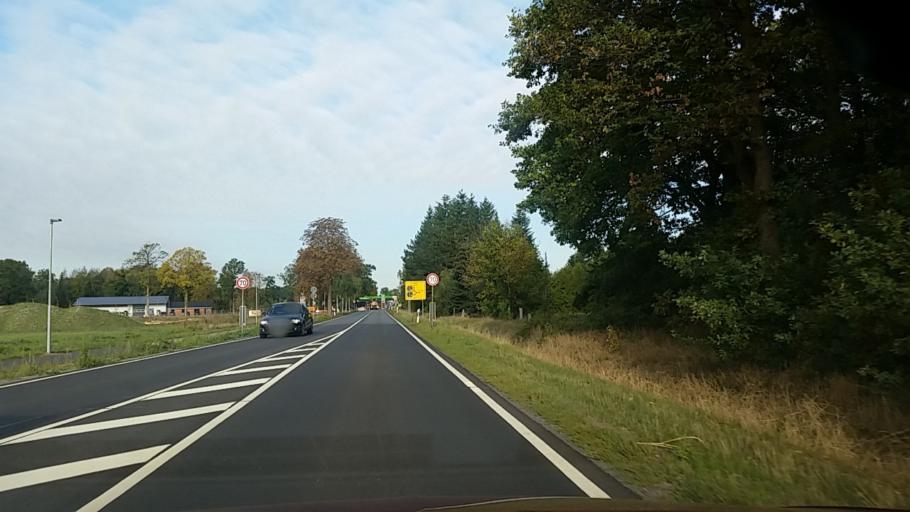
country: DE
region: Lower Saxony
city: Lachendorf
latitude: 52.6316
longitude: 10.2268
